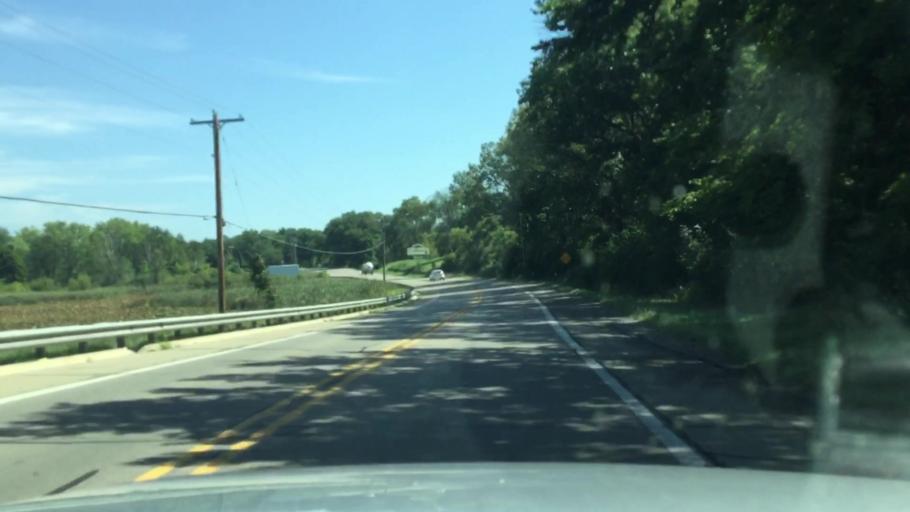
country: US
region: Michigan
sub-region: Washtenaw County
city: Manchester
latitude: 42.0670
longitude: -84.1022
